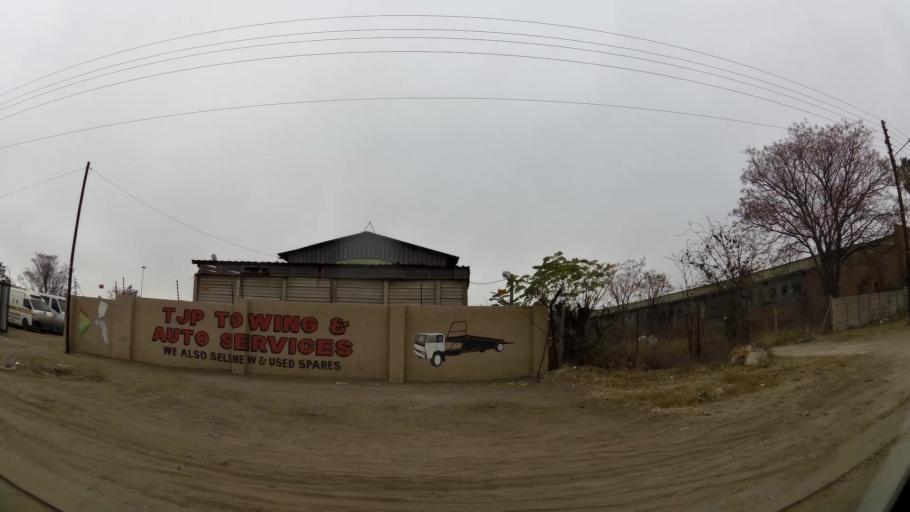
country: ZA
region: Limpopo
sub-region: Capricorn District Municipality
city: Polokwane
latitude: -23.8346
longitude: 29.3967
